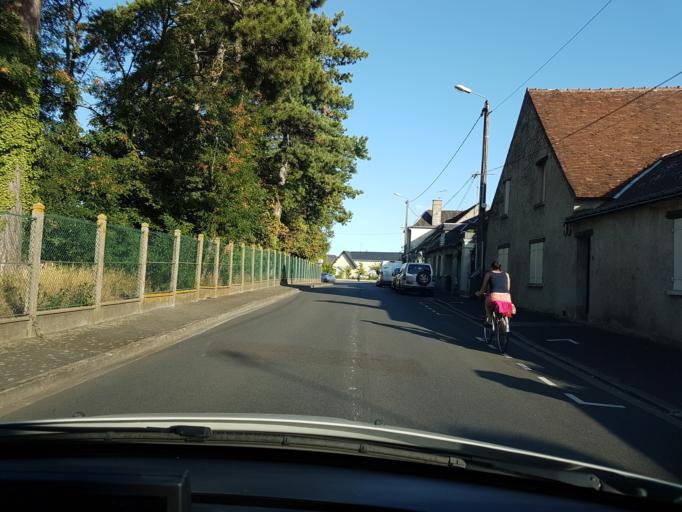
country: FR
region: Centre
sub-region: Departement d'Indre-et-Loire
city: Saint-Avertin
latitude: 47.3585
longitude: 0.7321
